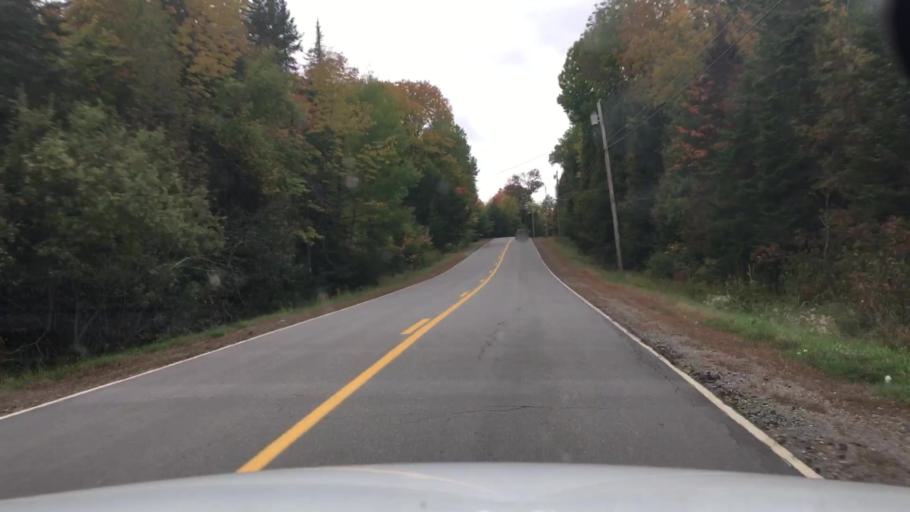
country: US
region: Maine
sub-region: Penobscot County
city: Hudson
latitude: 44.9844
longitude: -68.7863
